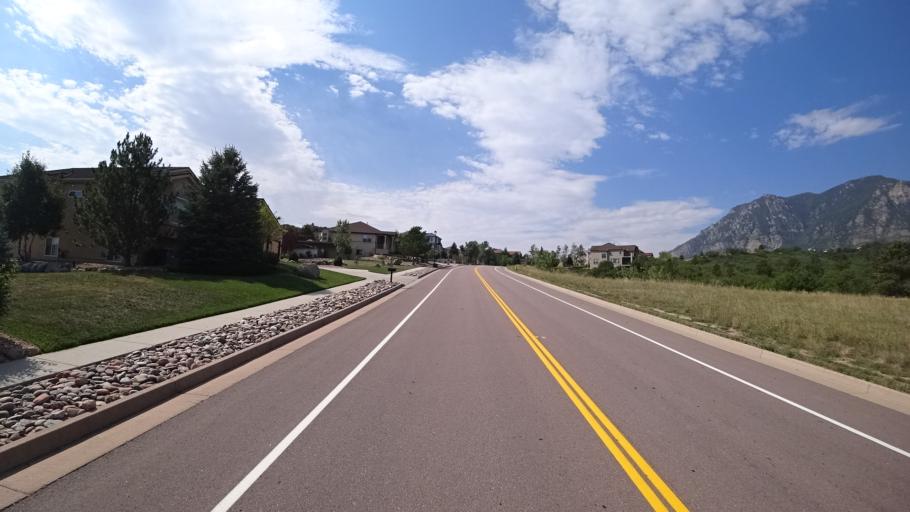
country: US
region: Colorado
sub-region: El Paso County
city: Fort Carson
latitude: 38.7599
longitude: -104.8195
